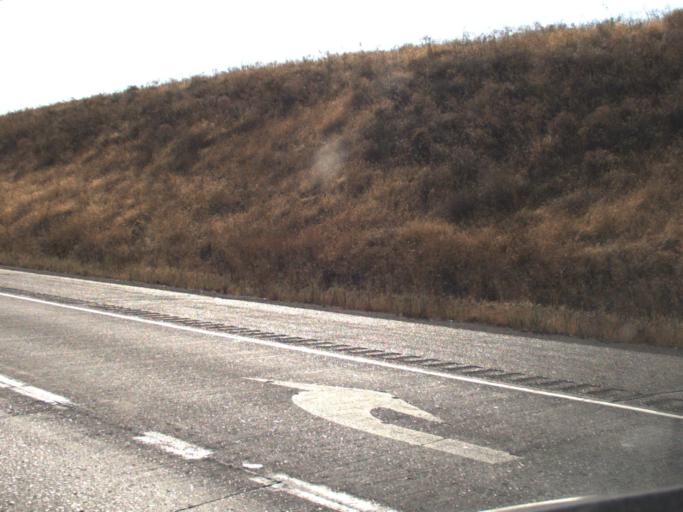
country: US
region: Washington
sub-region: Benton County
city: Highland
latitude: 46.1492
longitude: -119.2022
